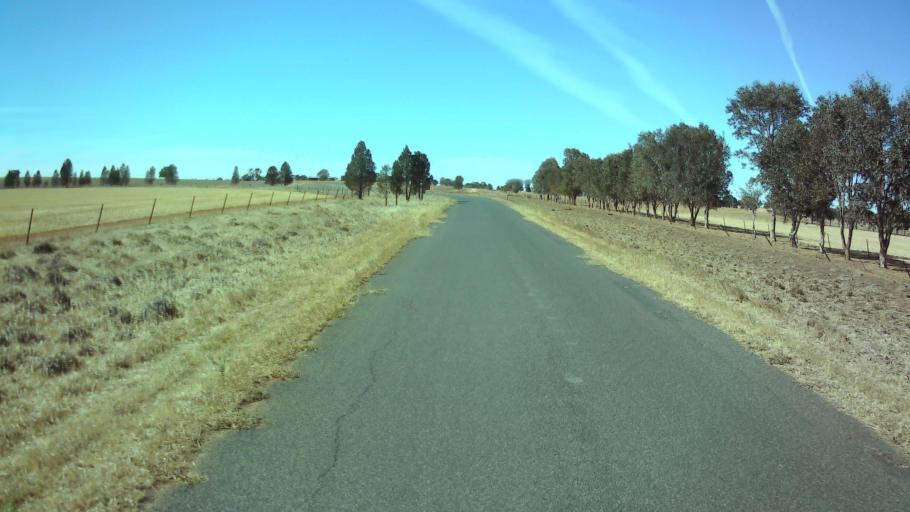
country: AU
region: New South Wales
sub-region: Weddin
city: Grenfell
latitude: -34.0468
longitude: 148.1736
